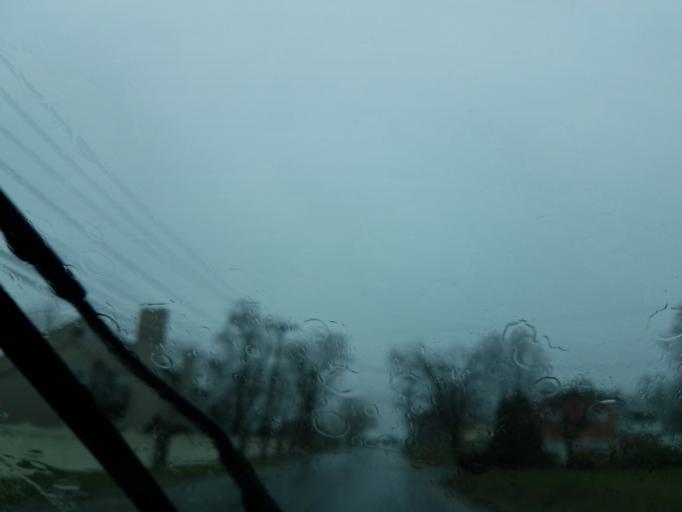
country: US
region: Connecticut
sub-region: New Haven County
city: Waterbury
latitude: 41.5255
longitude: -73.0655
